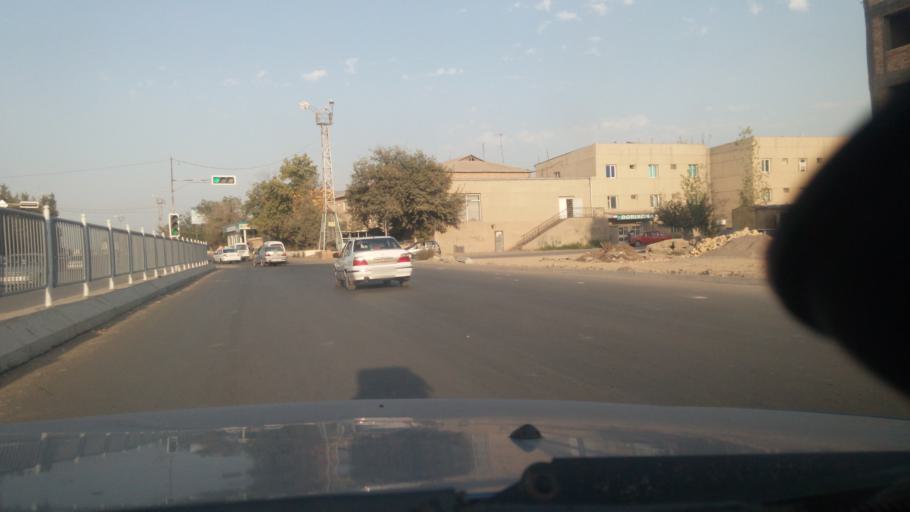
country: UZ
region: Sirdaryo
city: Guliston
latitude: 40.4932
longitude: 68.7862
